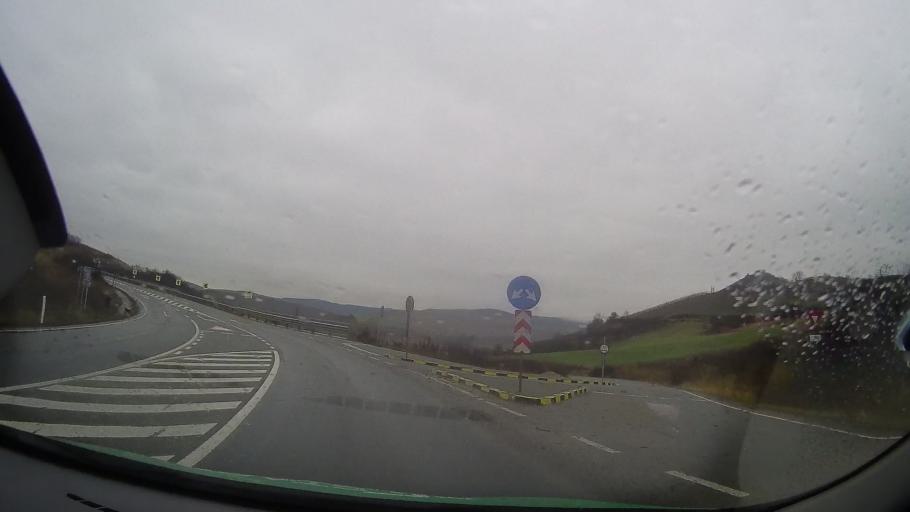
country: RO
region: Bistrita-Nasaud
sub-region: Comuna Teaca
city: Teaca
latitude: 46.9060
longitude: 24.4991
